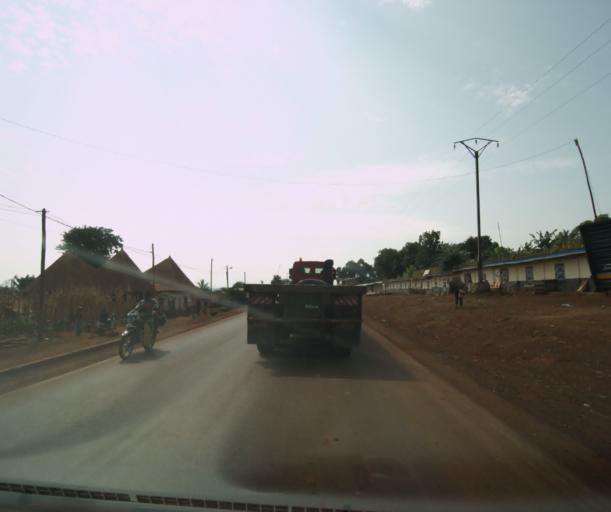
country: CM
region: West
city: Mbouda
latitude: 5.6203
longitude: 10.2690
